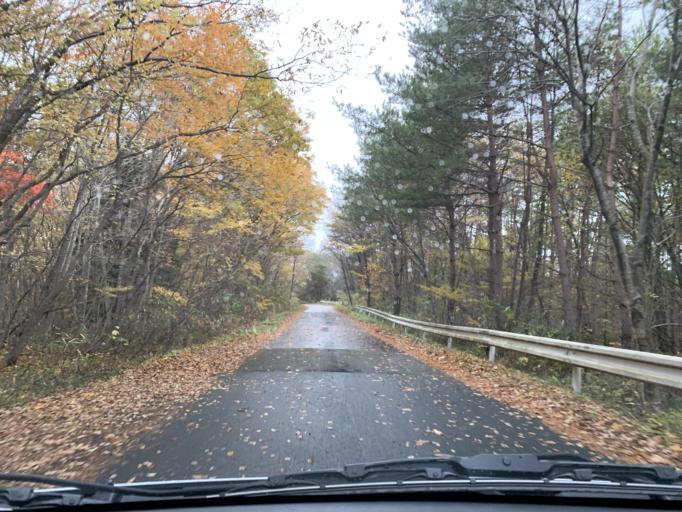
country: JP
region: Iwate
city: Mizusawa
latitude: 39.0757
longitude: 141.0284
